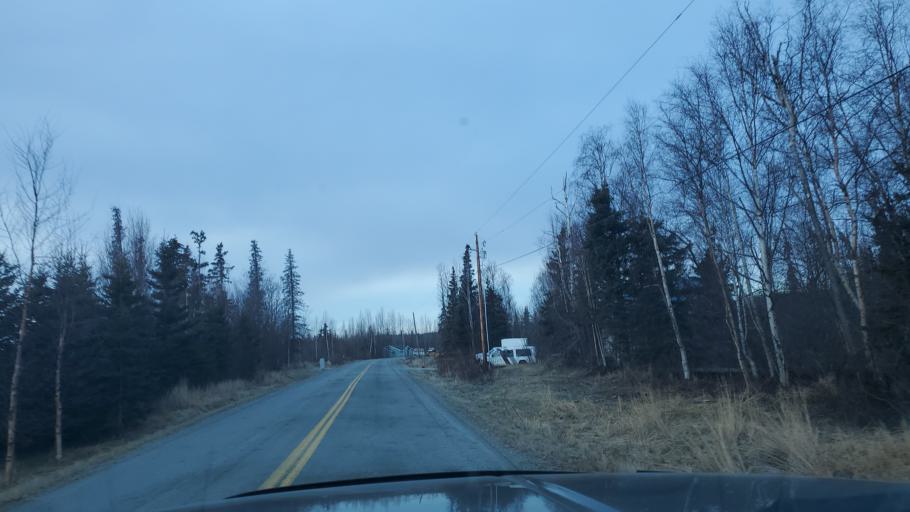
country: US
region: Alaska
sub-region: Matanuska-Susitna Borough
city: Lakes
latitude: 61.5724
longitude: -149.3308
